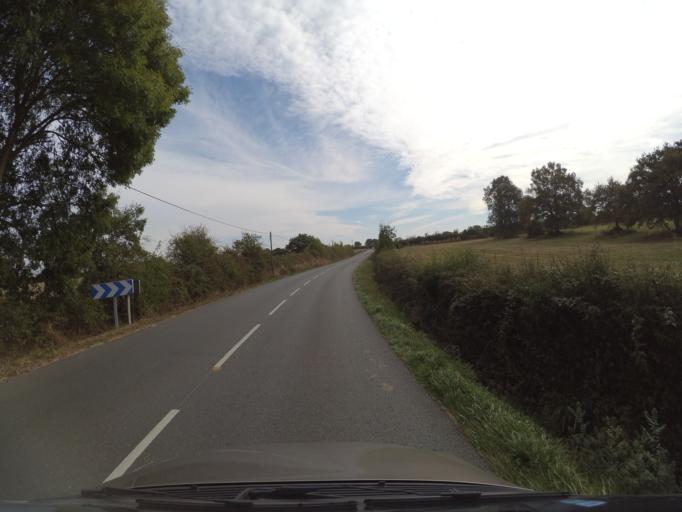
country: FR
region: Pays de la Loire
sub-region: Departement de Maine-et-Loire
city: Melay
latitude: 47.2096
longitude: -0.6758
